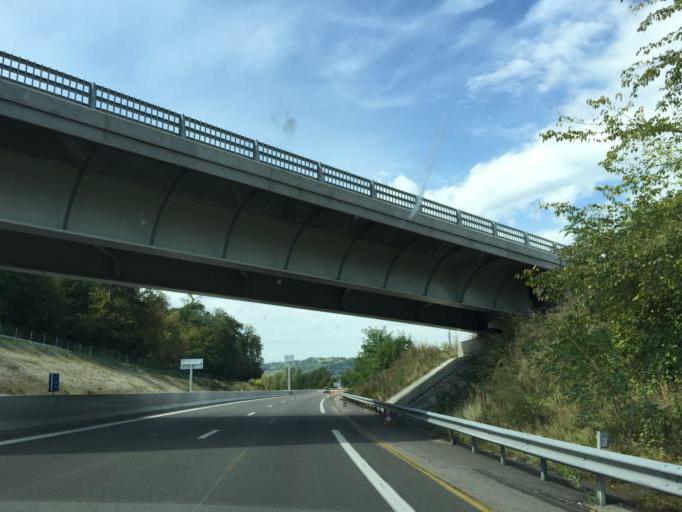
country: FR
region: Rhone-Alpes
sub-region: Departement de l'Isere
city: La Tour-du-Pin
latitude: 45.5596
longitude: 5.4457
